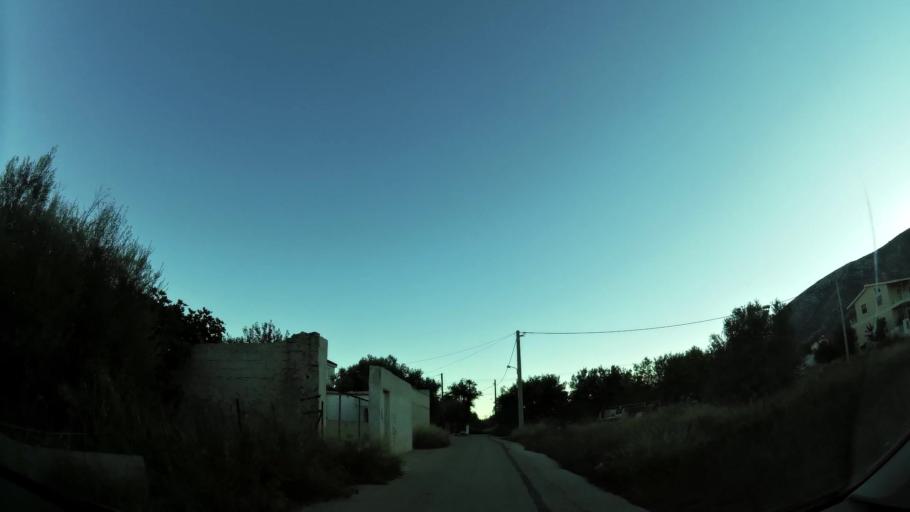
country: GR
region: Attica
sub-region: Nomarchia Anatolikis Attikis
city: Paiania
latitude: 37.9703
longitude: 23.8510
